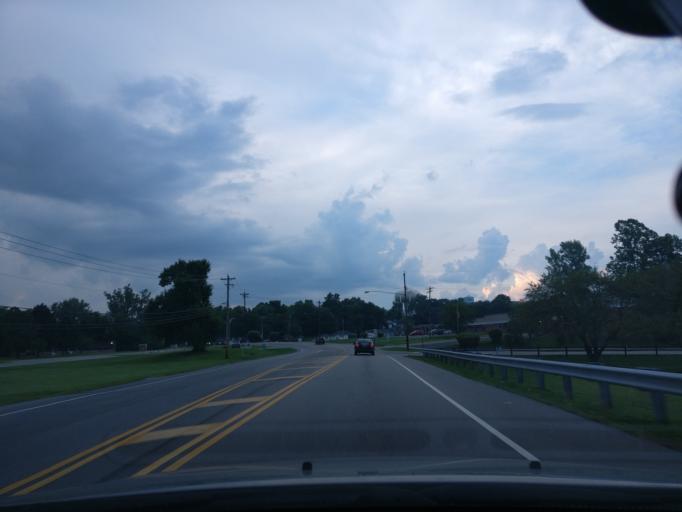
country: US
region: Ohio
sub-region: Warren County
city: Franklin
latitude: 39.5534
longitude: -84.2991
